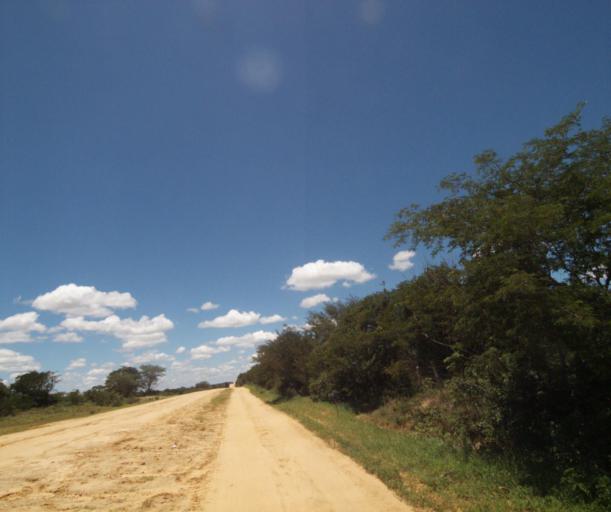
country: BR
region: Bahia
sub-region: Carinhanha
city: Carinhanha
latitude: -14.2863
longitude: -43.7851
